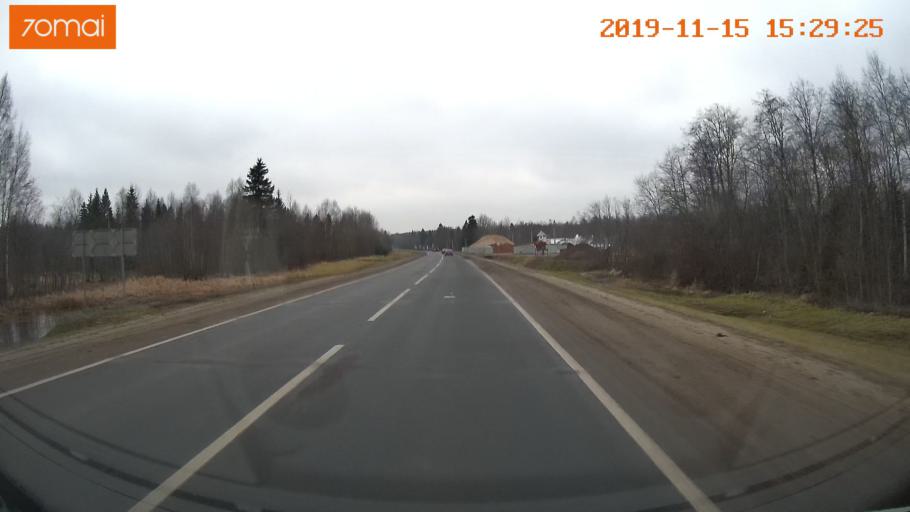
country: RU
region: Jaroslavl
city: Danilov
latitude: 58.1210
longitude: 40.1204
